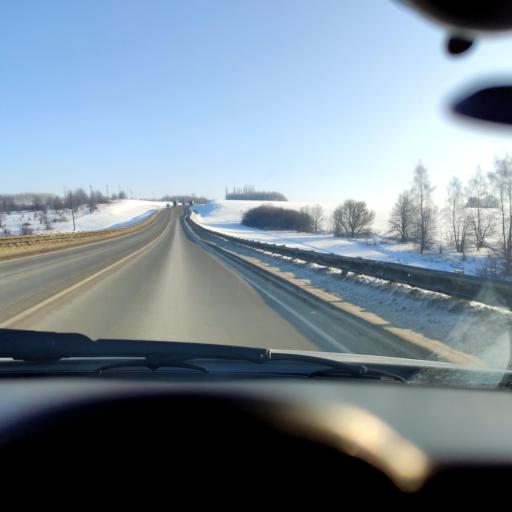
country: RU
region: Kursk
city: Shchigry
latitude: 51.6551
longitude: 36.9033
